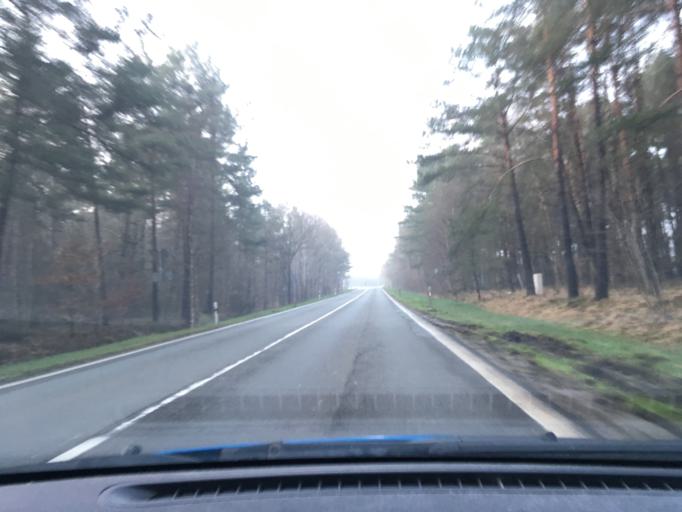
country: DE
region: Lower Saxony
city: Soltau
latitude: 52.9471
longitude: 9.8790
